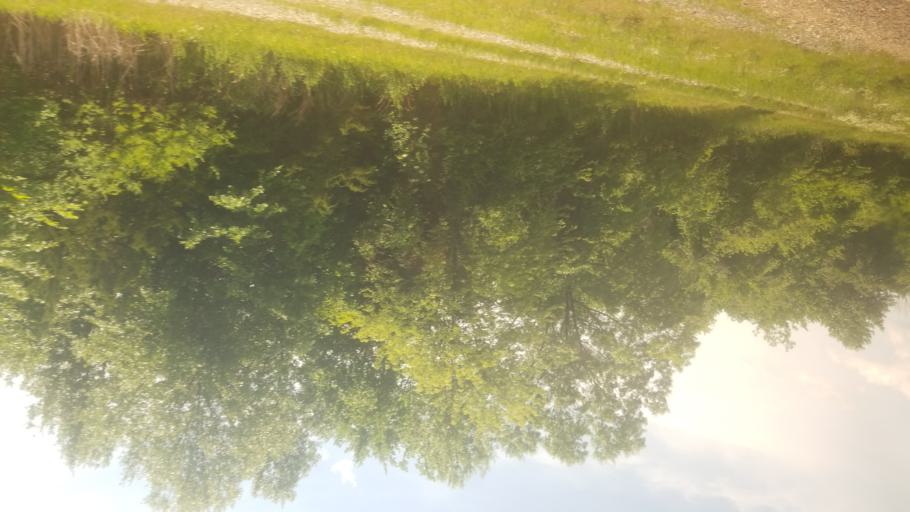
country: US
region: Missouri
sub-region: Macon County
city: La Plata
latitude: 40.0302
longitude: -92.4879
